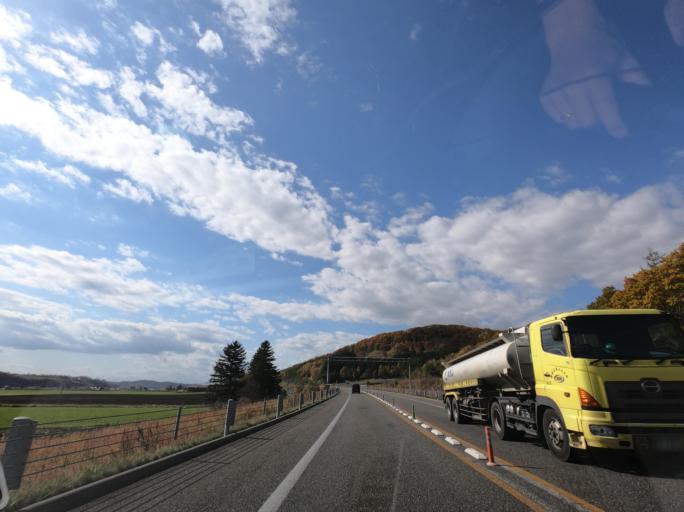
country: JP
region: Hokkaido
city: Otofuke
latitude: 43.1204
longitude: 143.6551
